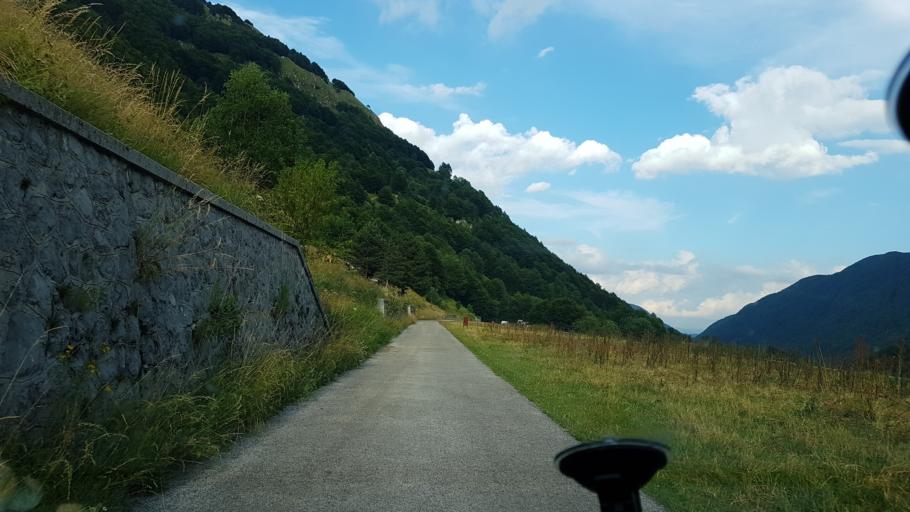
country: IT
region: Friuli Venezia Giulia
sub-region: Provincia di Udine
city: Prato
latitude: 46.3358
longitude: 13.3266
